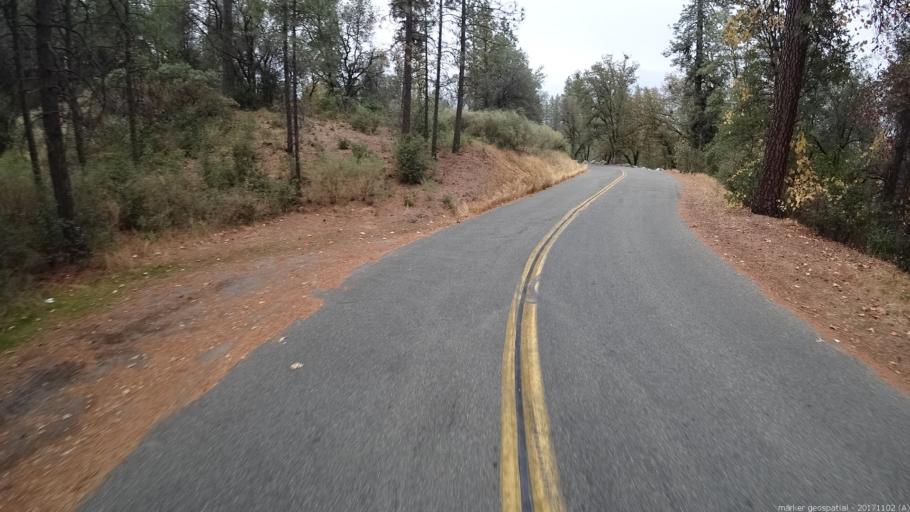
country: US
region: California
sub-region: Shasta County
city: Bella Vista
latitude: 40.7398
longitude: -122.2393
